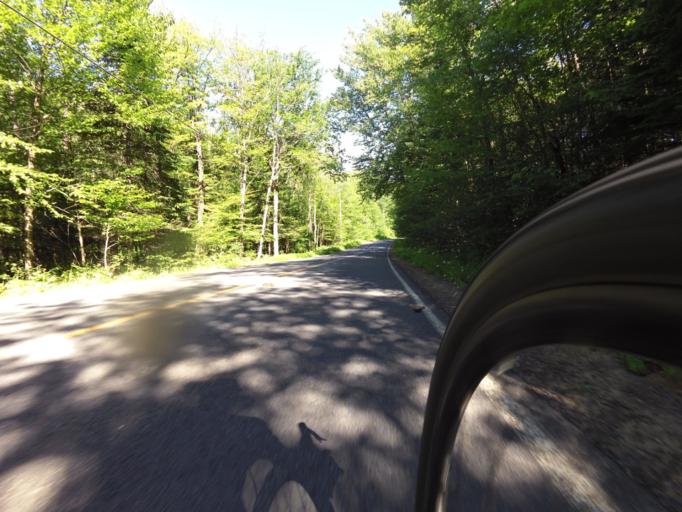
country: CA
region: Quebec
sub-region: Laurentides
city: Brownsburg-Chatham
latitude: 45.8922
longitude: -74.5946
